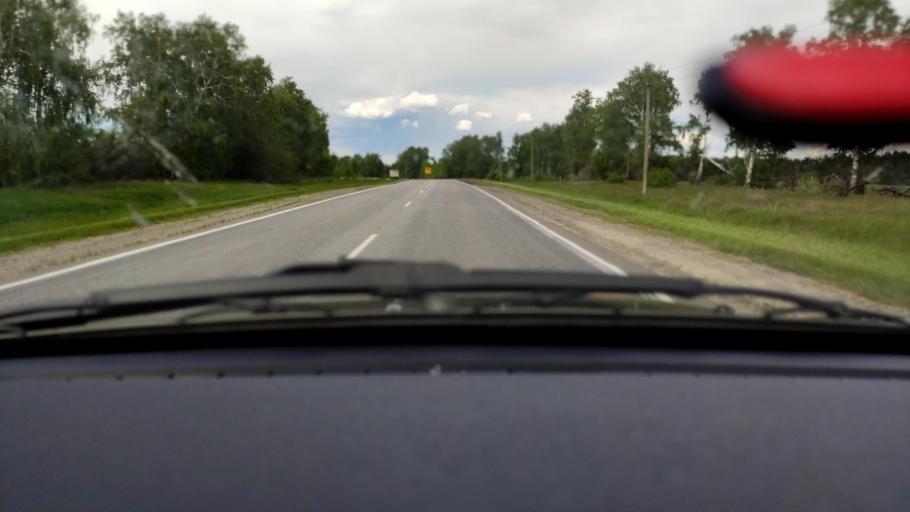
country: RU
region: Voronezj
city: Uryv-Pokrovka
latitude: 51.0633
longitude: 38.9939
